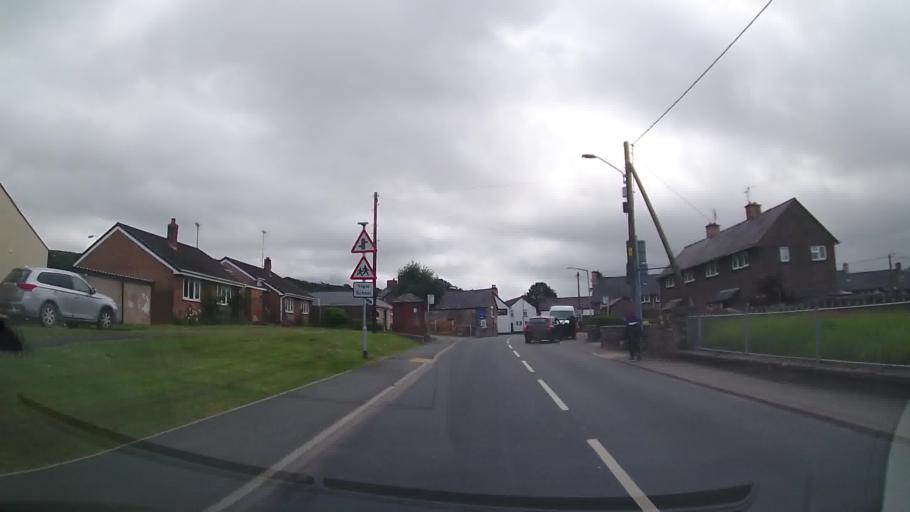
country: GB
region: Wales
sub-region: Denbighshire
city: Corwen
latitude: 52.9598
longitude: -3.4040
